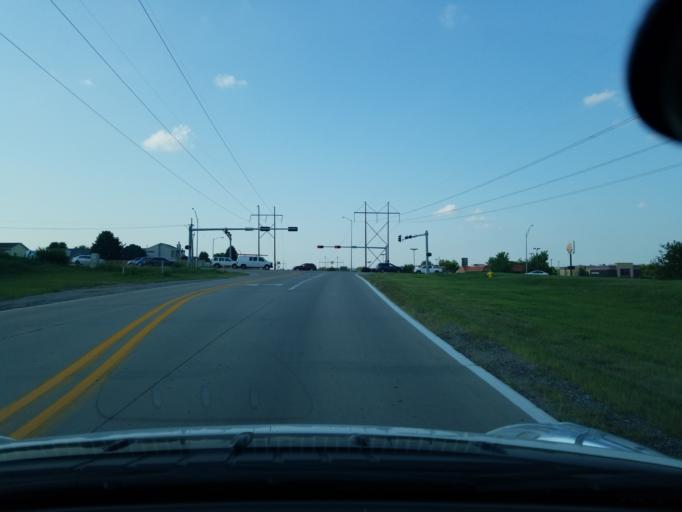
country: US
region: Nebraska
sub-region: Sarpy County
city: Offutt Air Force Base
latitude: 41.1393
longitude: -95.9762
